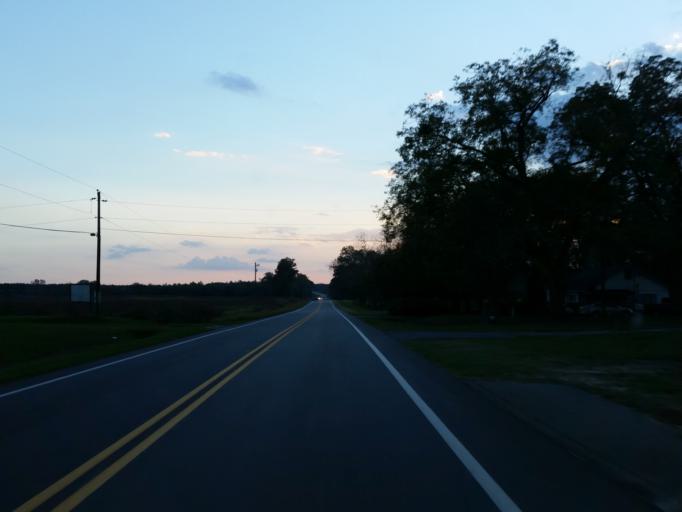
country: US
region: Georgia
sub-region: Pulaski County
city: Hawkinsville
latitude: 32.2638
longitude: -83.4862
